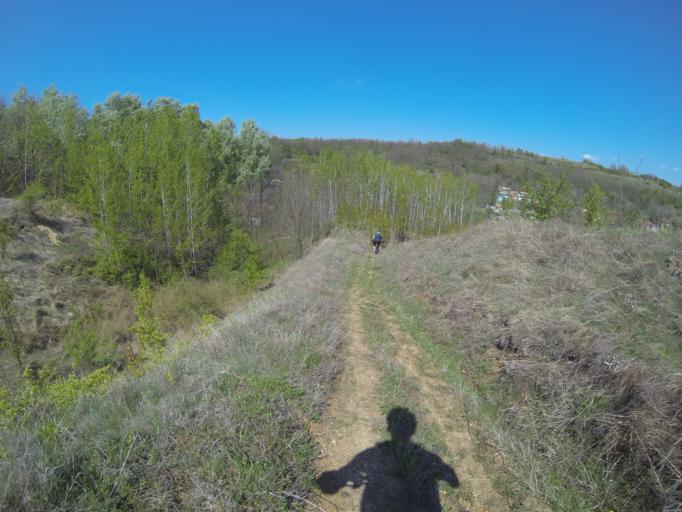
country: RO
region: Gorj
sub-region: Comuna Crusetu
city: Crusetu
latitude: 44.5918
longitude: 23.6575
